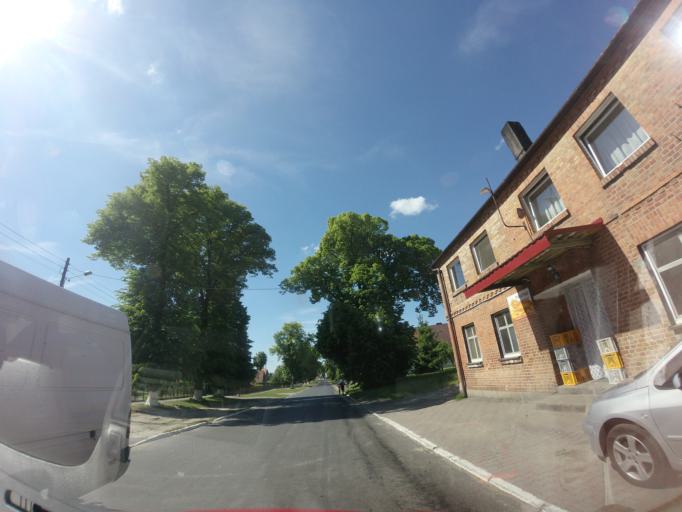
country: PL
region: West Pomeranian Voivodeship
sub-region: Powiat choszczenski
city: Recz
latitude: 53.1865
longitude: 15.5868
